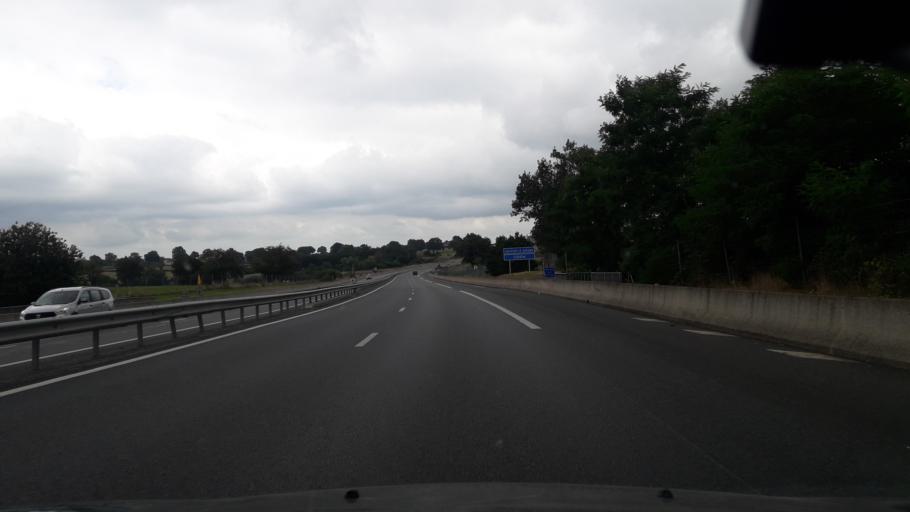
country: FR
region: Auvergne
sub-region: Departement de l'Allier
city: Desertines
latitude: 46.3776
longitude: 2.6785
